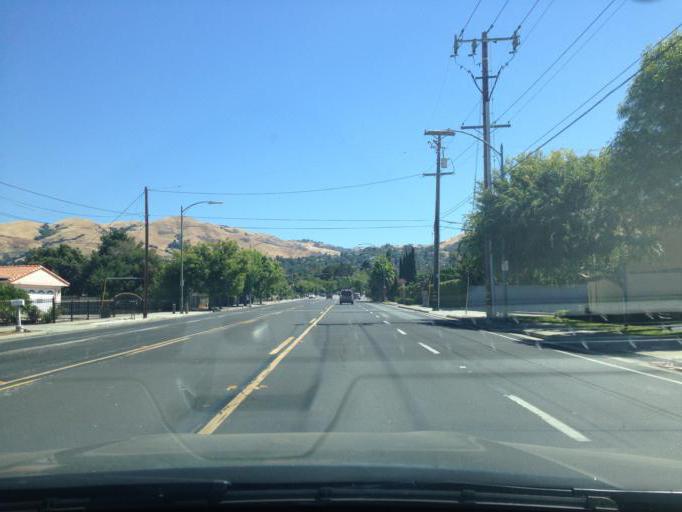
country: US
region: California
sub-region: Santa Clara County
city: East Foothills
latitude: 37.3790
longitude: -121.8297
